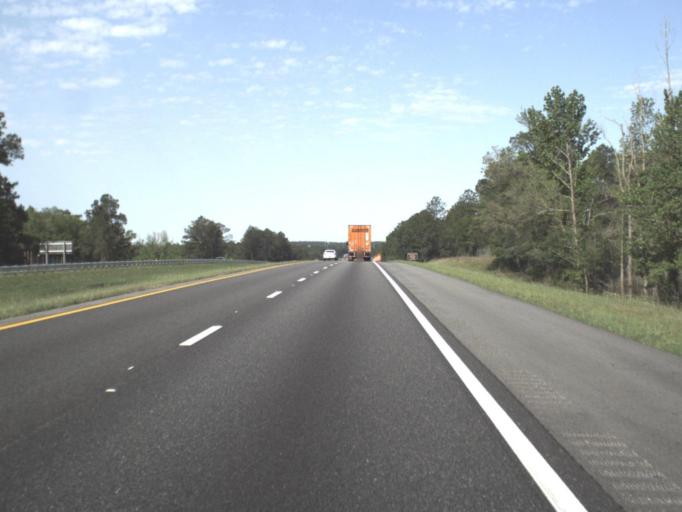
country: US
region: Florida
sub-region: Walton County
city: DeFuniak Springs
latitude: 30.7216
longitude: -85.9172
